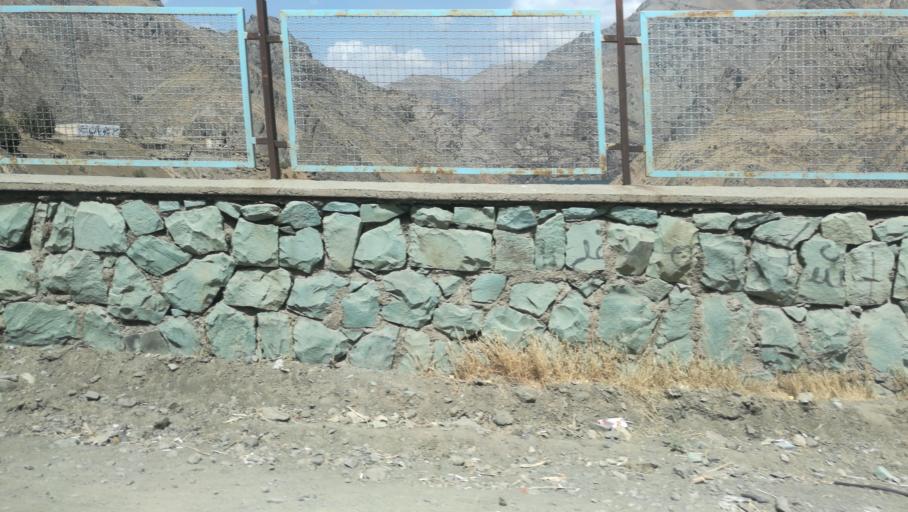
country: IR
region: Alborz
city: Karaj
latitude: 35.9776
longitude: 51.0942
